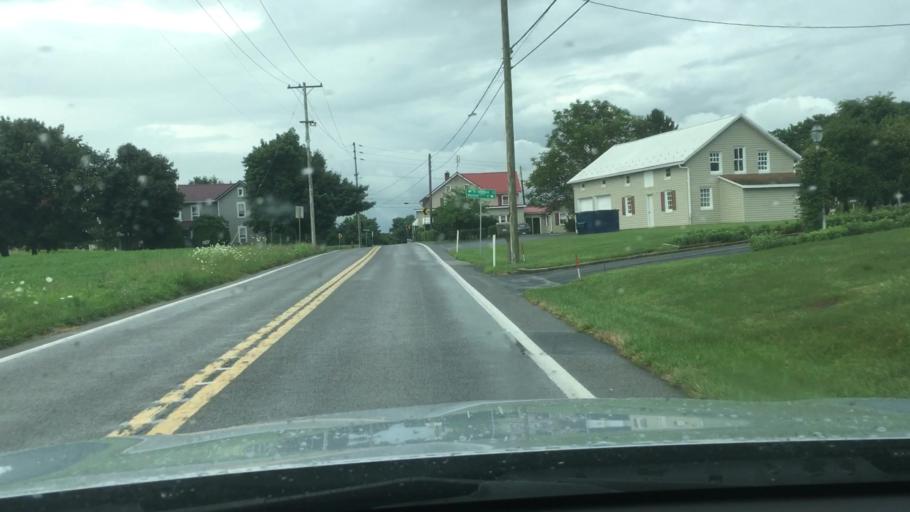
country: US
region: Pennsylvania
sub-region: Franklin County
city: Chambersburg
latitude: 39.8880
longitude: -77.7234
